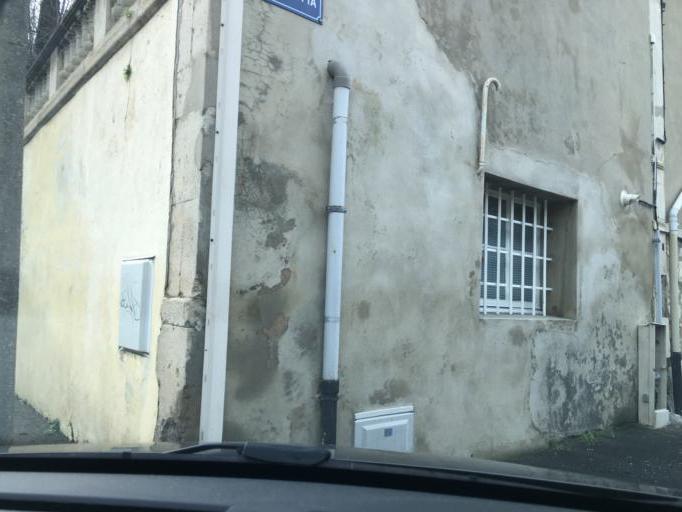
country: FR
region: Provence-Alpes-Cote d'Azur
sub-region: Departement du Vaucluse
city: Avignon
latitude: 43.9362
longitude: 4.8041
